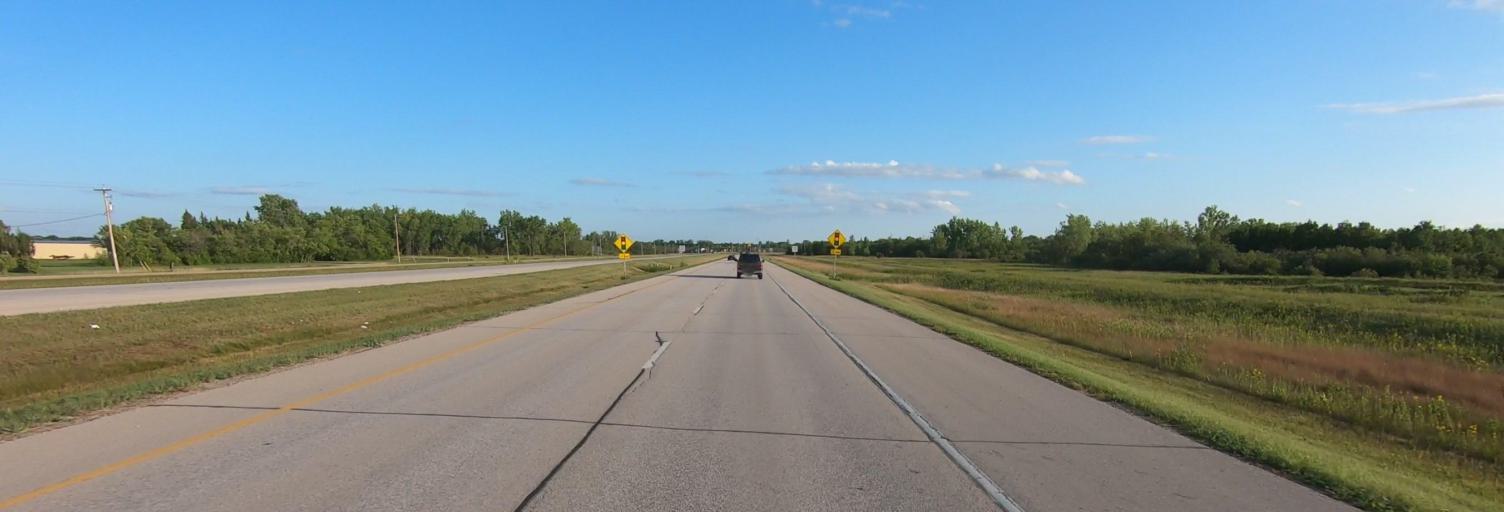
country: CA
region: Manitoba
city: Selkirk
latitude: 49.9816
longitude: -96.9749
